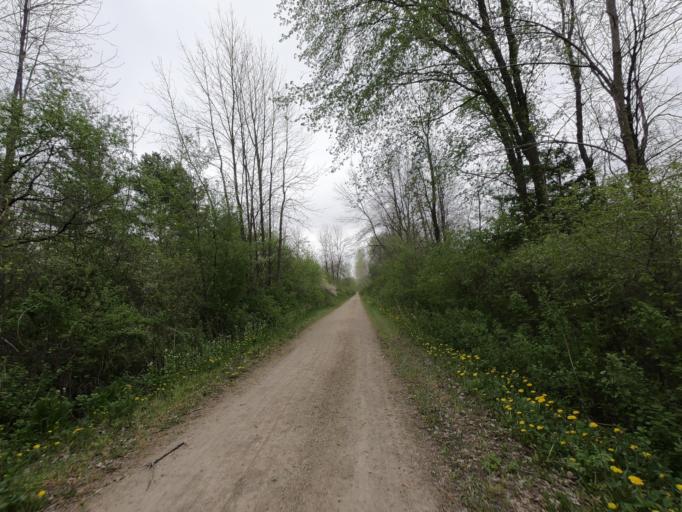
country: US
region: Wisconsin
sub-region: Jefferson County
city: Johnson Creek
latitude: 43.0321
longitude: -88.7496
